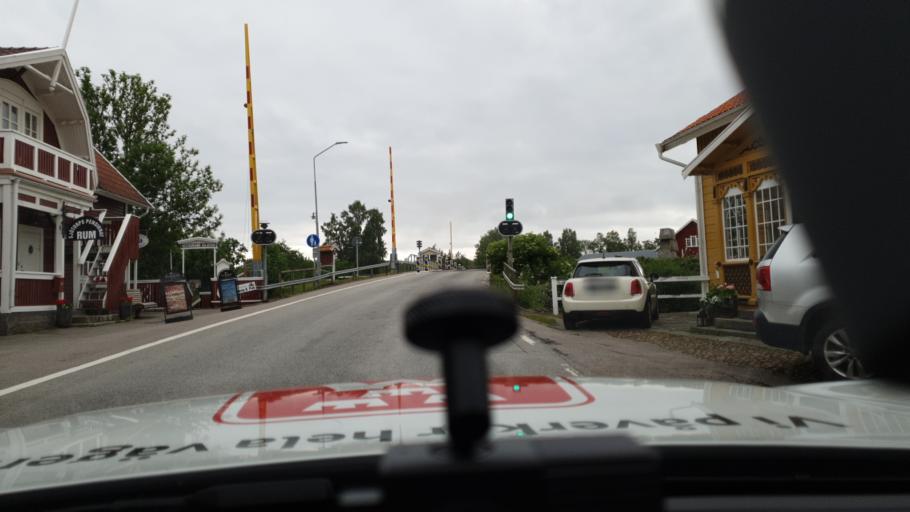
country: SE
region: Vaestra Goetaland
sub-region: Gullspangs Kommun
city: Gullspang
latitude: 58.8358
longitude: 13.9806
